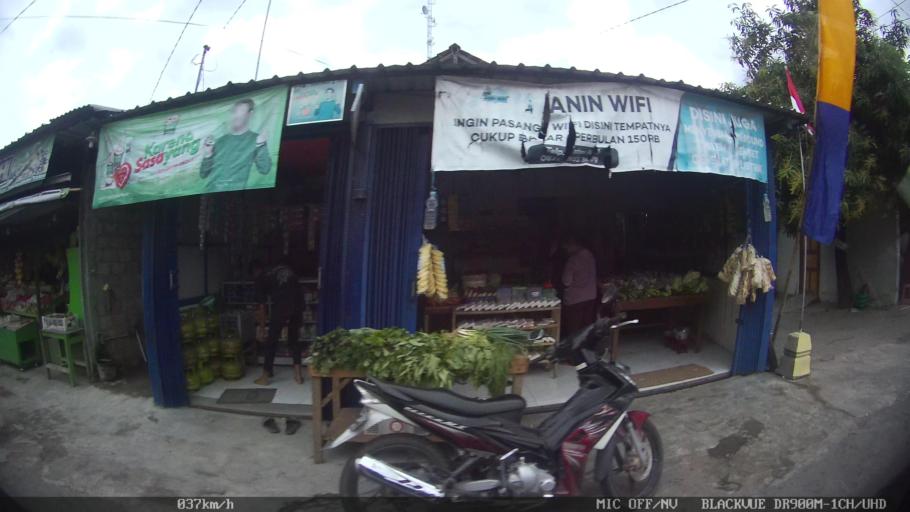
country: ID
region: Daerah Istimewa Yogyakarta
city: Sewon
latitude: -7.8610
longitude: 110.4089
